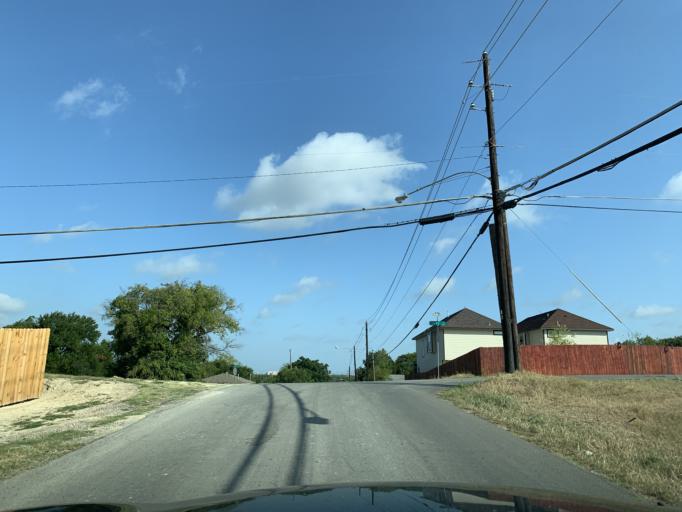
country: US
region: Texas
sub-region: Dallas County
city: Hutchins
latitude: 32.6751
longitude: -96.7765
